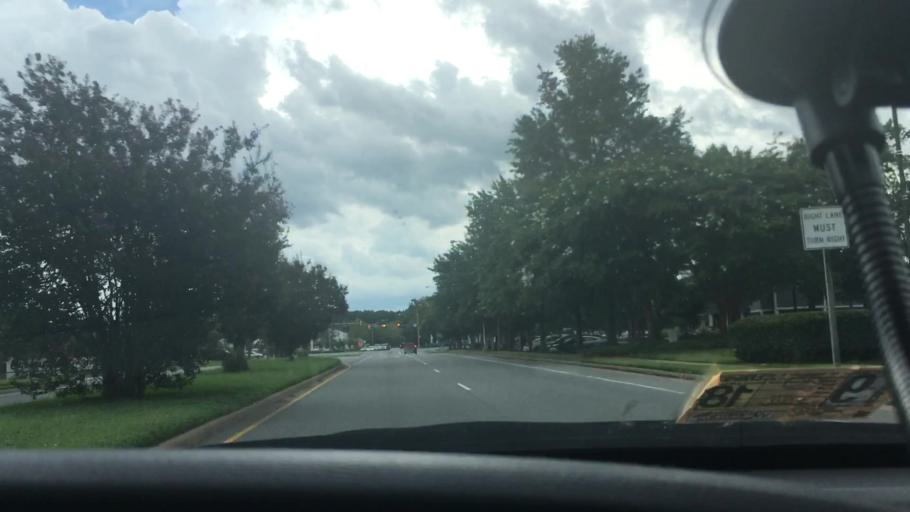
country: US
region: Virginia
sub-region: City of Portsmouth
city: Portsmouth Heights
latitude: 36.8261
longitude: -76.4097
